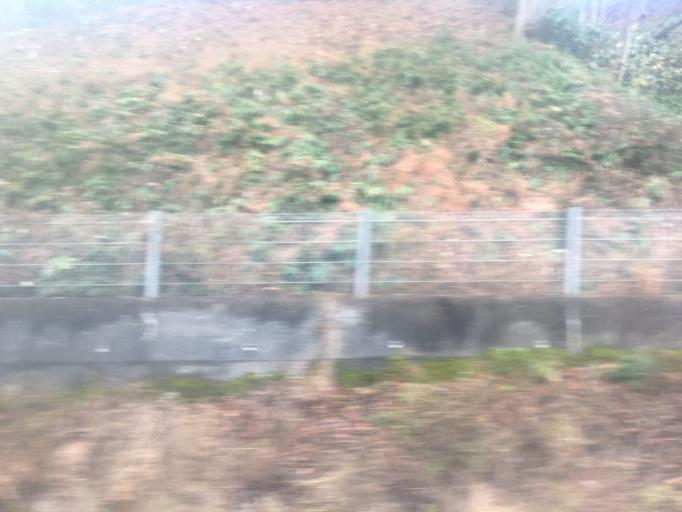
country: JP
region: Akita
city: Takanosu
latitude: 40.2625
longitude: 140.4091
